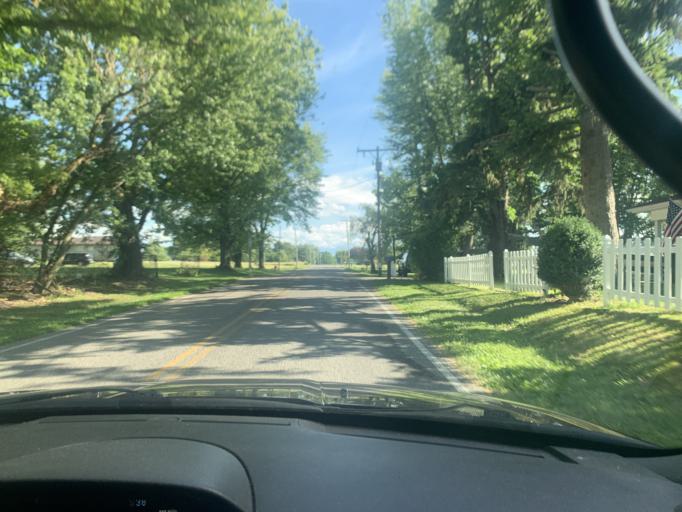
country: US
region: Ohio
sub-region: Logan County
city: Bellefontaine
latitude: 40.3463
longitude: -83.8195
